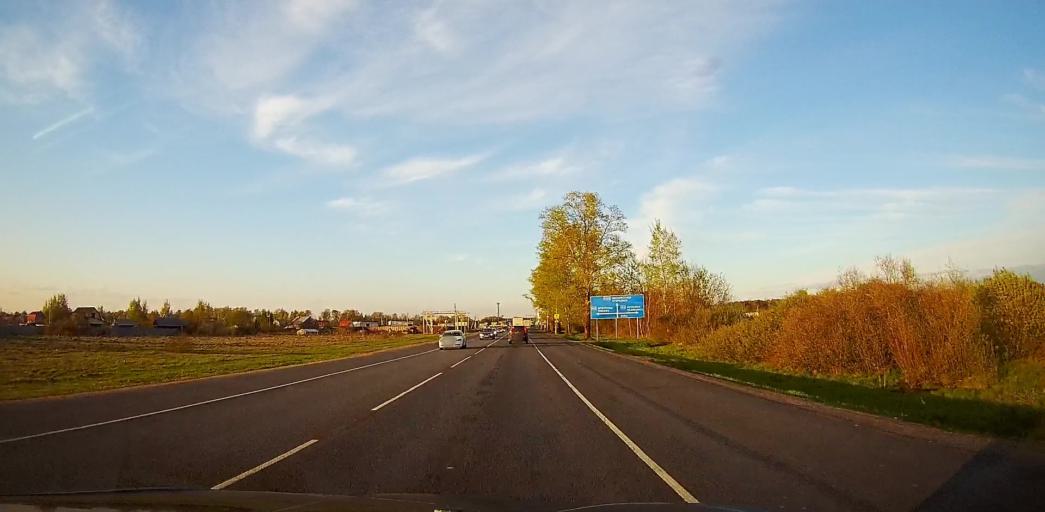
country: RU
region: Moskovskaya
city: Troitskoye
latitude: 55.2757
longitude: 38.4884
